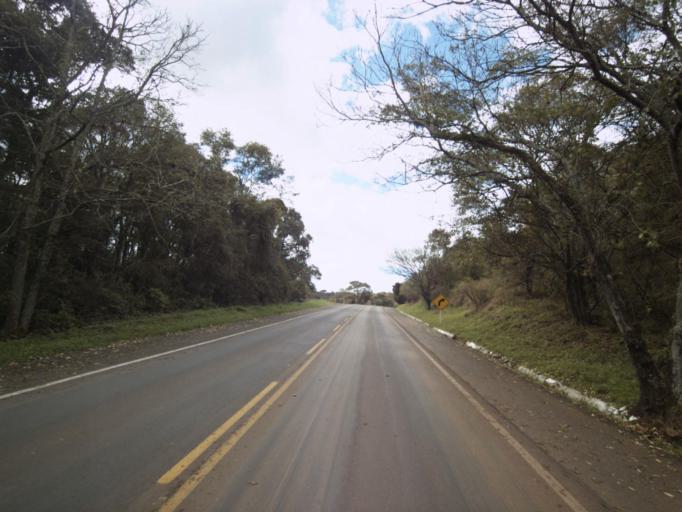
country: BR
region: Santa Catarina
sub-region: Concordia
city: Concordia
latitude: -27.3386
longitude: -51.9816
